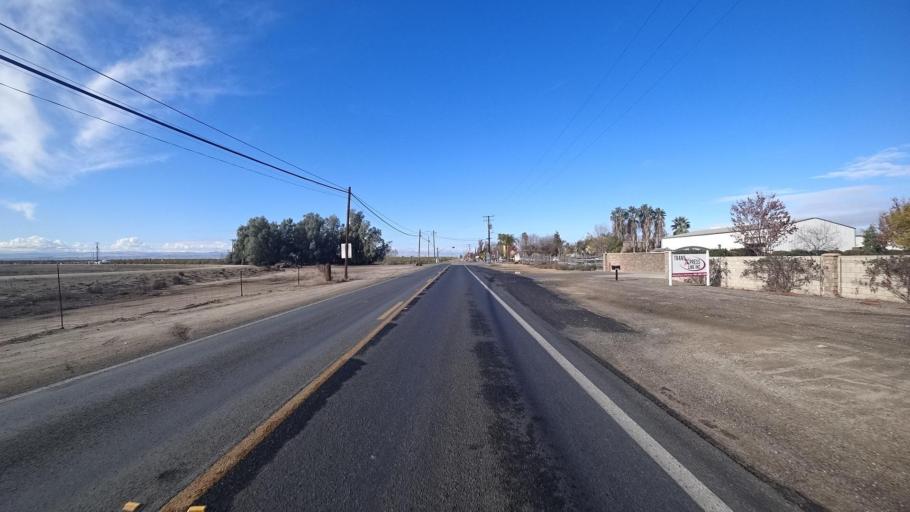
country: US
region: California
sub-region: Kern County
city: Rosedale
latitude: 35.3835
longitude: -119.2502
